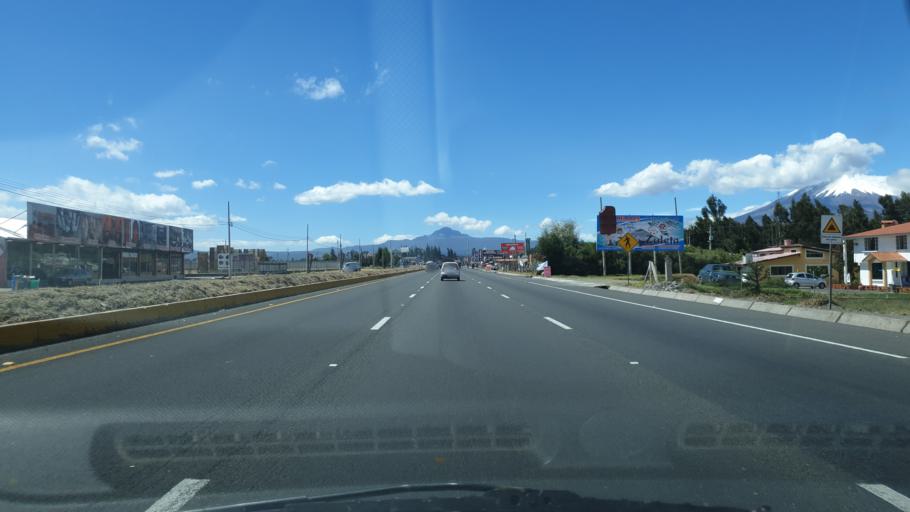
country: EC
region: Cotopaxi
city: Saquisili
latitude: -0.8079
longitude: -78.6229
